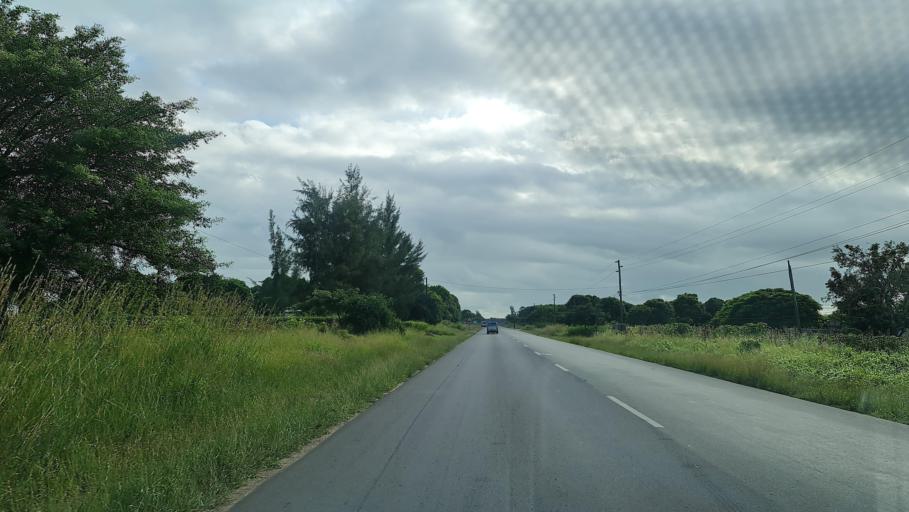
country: MZ
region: Maputo
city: Manhica
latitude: -25.4165
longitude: 32.7349
